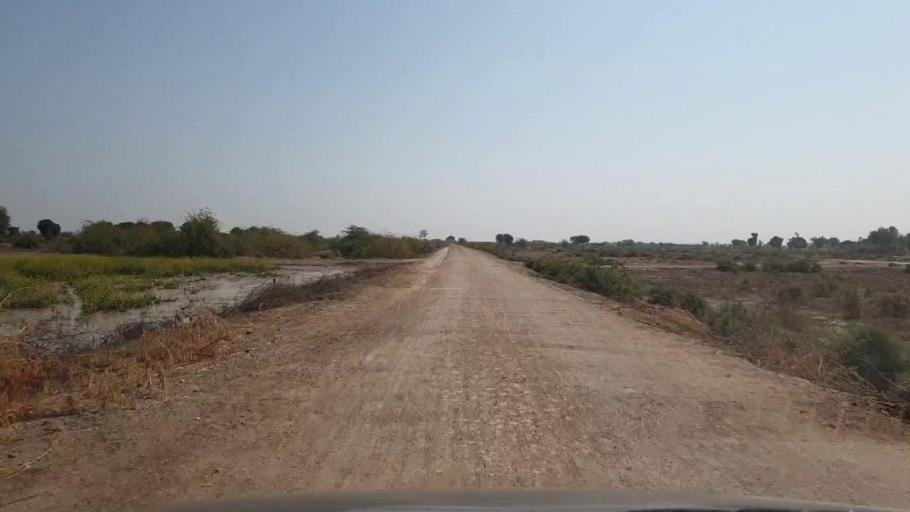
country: PK
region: Sindh
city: Samaro
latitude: 25.2497
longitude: 69.2808
